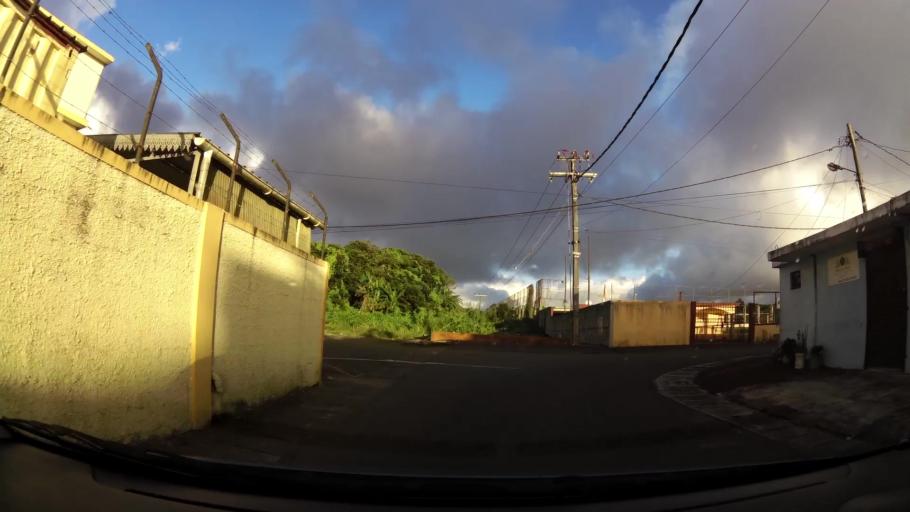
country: MU
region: Plaines Wilhems
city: Curepipe
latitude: -20.3099
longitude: 57.5378
